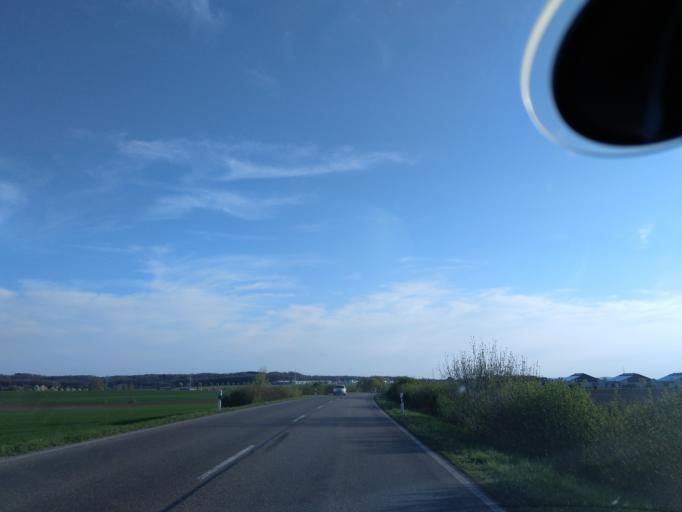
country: DE
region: Baden-Wuerttemberg
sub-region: Regierungsbezirk Stuttgart
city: Ilshofen
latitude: 49.1686
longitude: 9.9576
